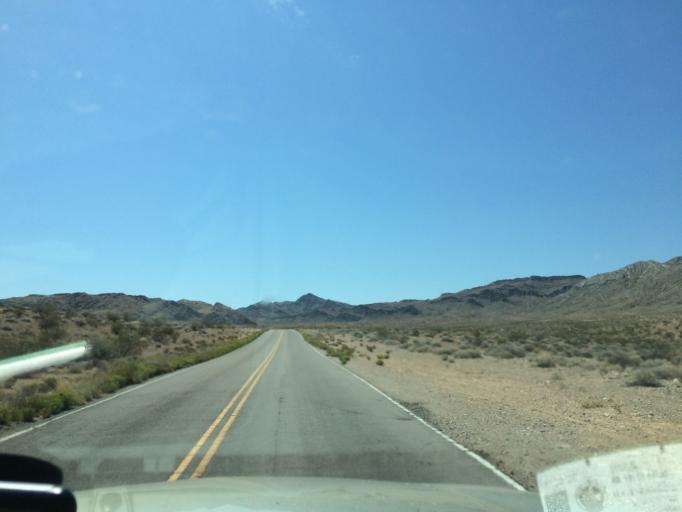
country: US
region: Nevada
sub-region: Clark County
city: Moapa Valley
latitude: 36.4368
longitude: -114.6405
